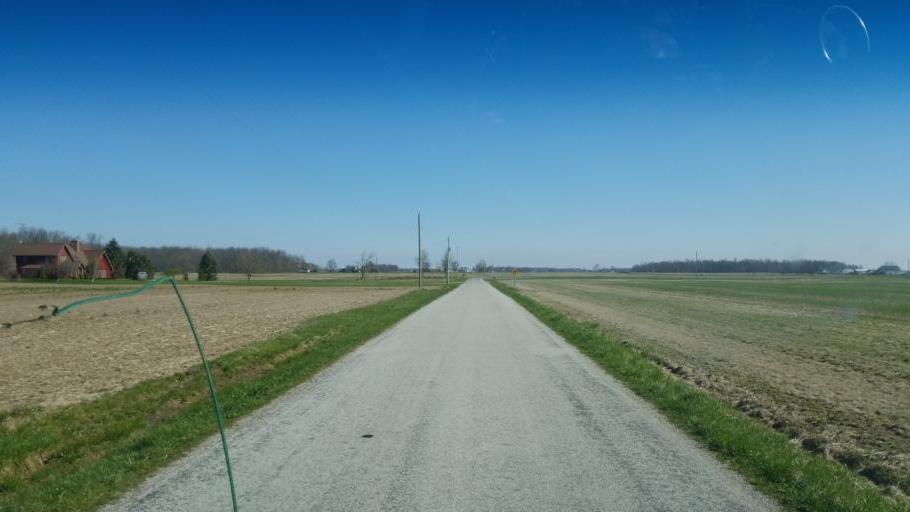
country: US
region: Ohio
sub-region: Hardin County
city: Kenton
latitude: 40.6784
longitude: -83.5615
